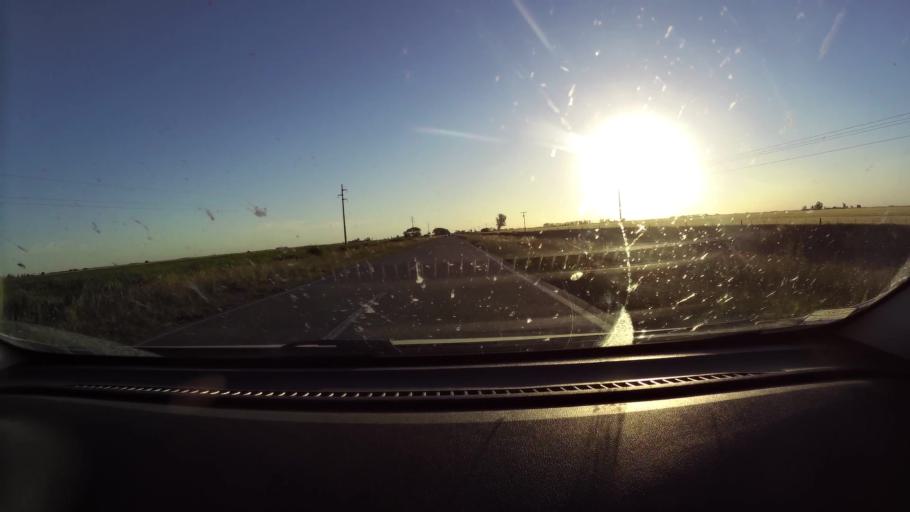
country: AR
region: Cordoba
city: Pozo del Molle
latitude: -32.0577
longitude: -62.9735
